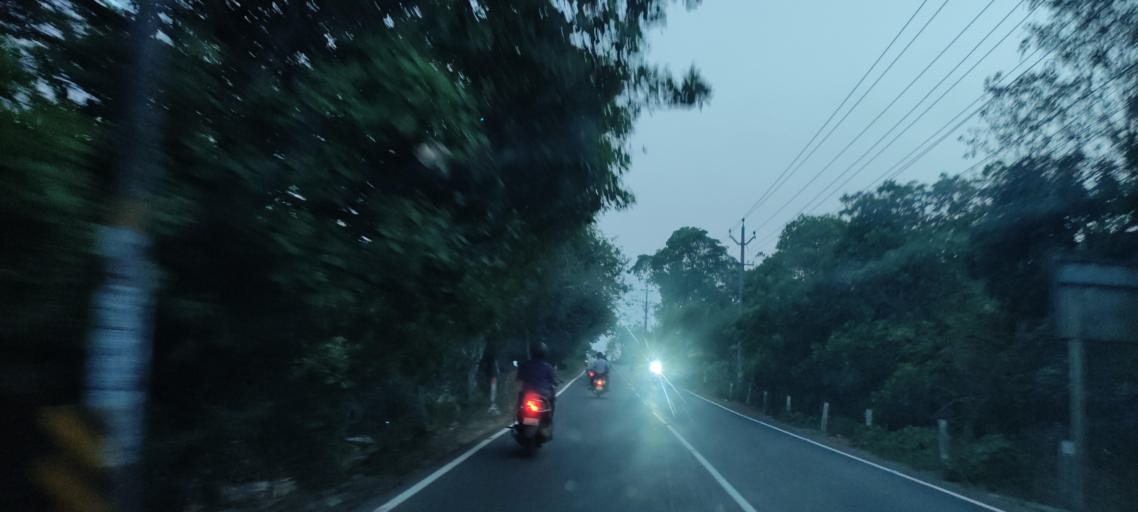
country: IN
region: Kerala
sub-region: Alappuzha
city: Mavelikara
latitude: 9.3276
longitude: 76.4620
